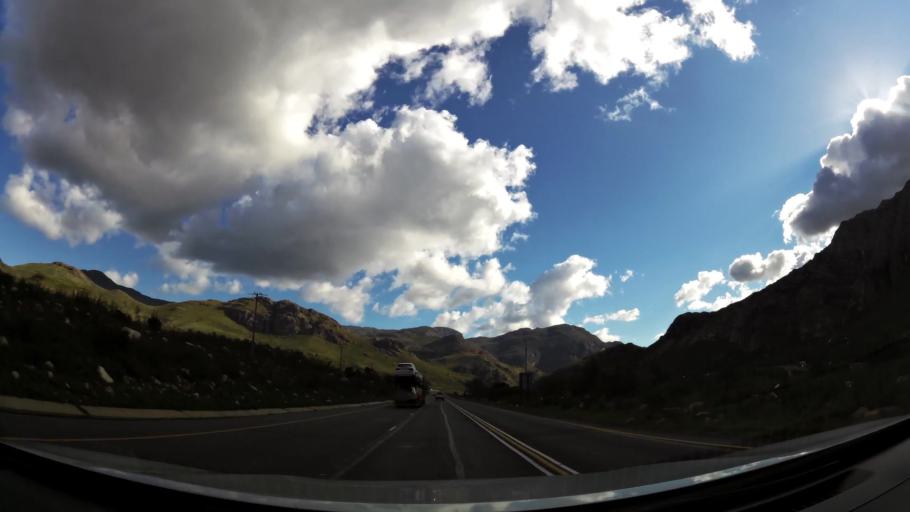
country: ZA
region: Western Cape
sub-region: Cape Winelands District Municipality
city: Paarl
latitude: -33.7274
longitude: 19.1374
